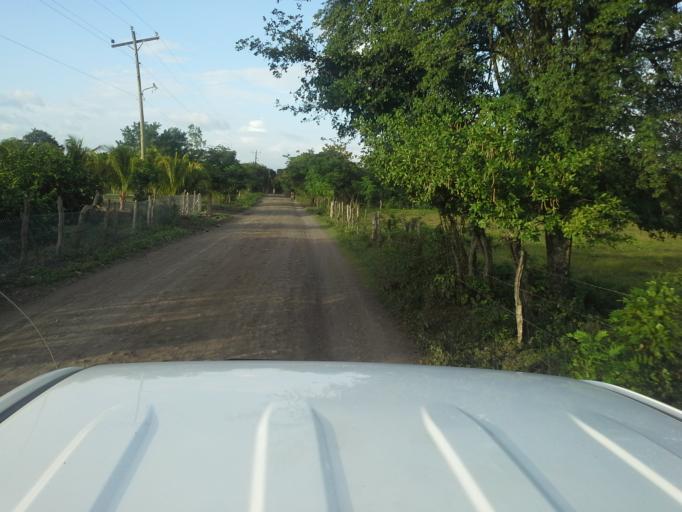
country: NI
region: Matagalpa
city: Ciudad Dario
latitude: 12.7950
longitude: -86.1491
